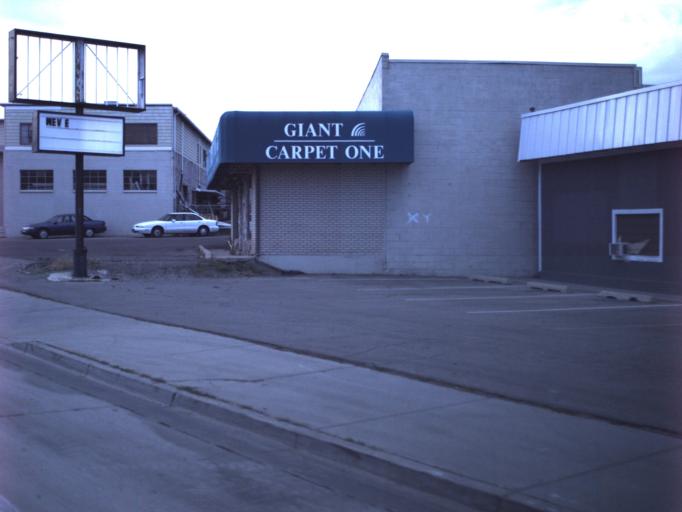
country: US
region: Utah
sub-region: Utah County
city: Orem
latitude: 40.2642
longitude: -111.6795
